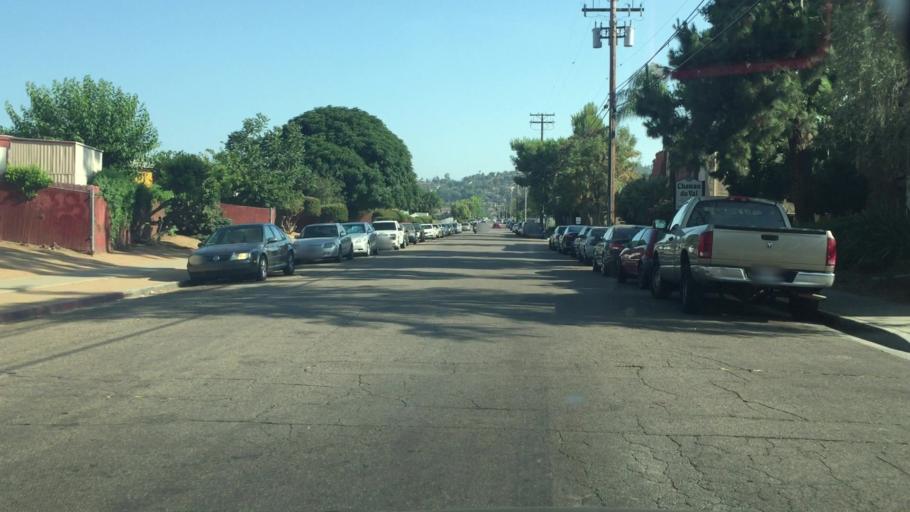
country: US
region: California
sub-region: San Diego County
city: El Cajon
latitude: 32.7913
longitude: -116.9482
